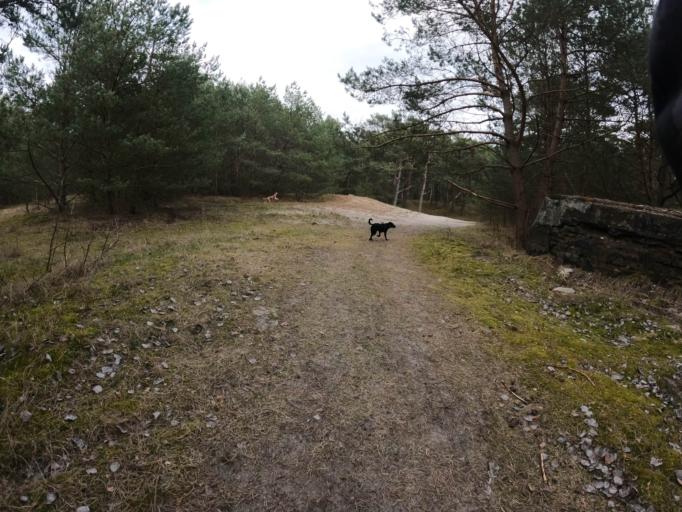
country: PL
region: West Pomeranian Voivodeship
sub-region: Powiat gryficki
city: Mrzezyno
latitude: 54.1350
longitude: 15.2530
